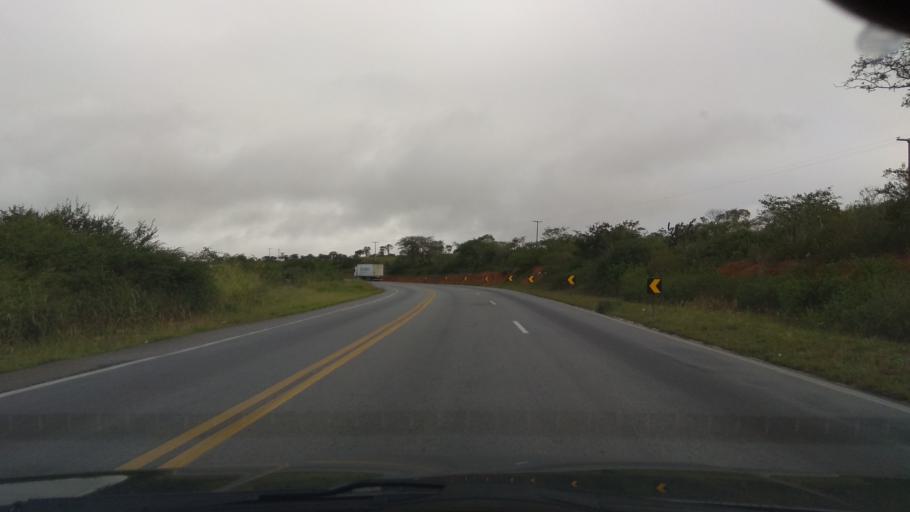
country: BR
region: Bahia
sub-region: Santa Ines
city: Santa Ines
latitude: -13.0516
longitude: -39.9600
